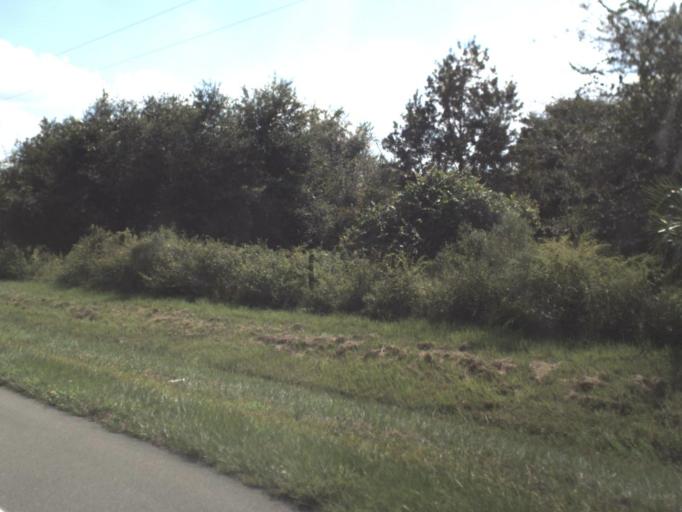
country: US
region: Florida
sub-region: Hardee County
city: Zolfo Springs
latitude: 27.4861
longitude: -81.7390
